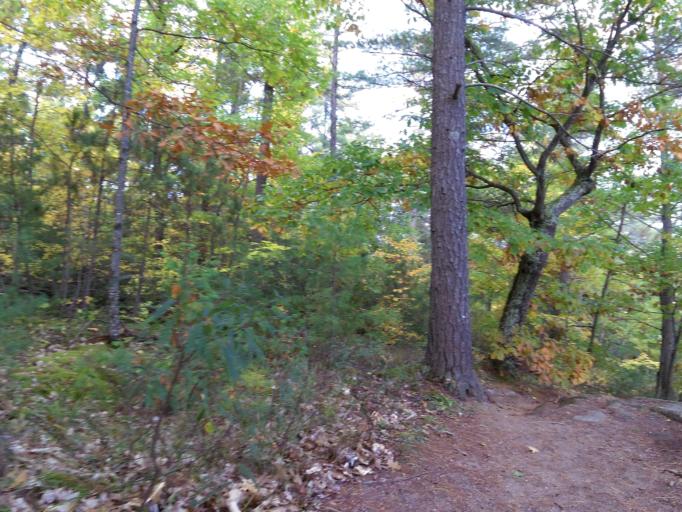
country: CA
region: Ontario
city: Deep River
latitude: 45.8862
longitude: -77.6334
